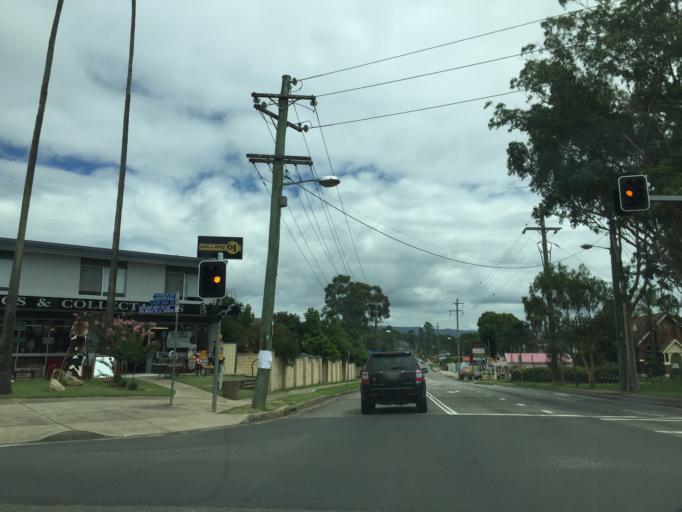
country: AU
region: New South Wales
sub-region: Hawkesbury
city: Richmond
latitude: -33.5799
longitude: 150.7196
